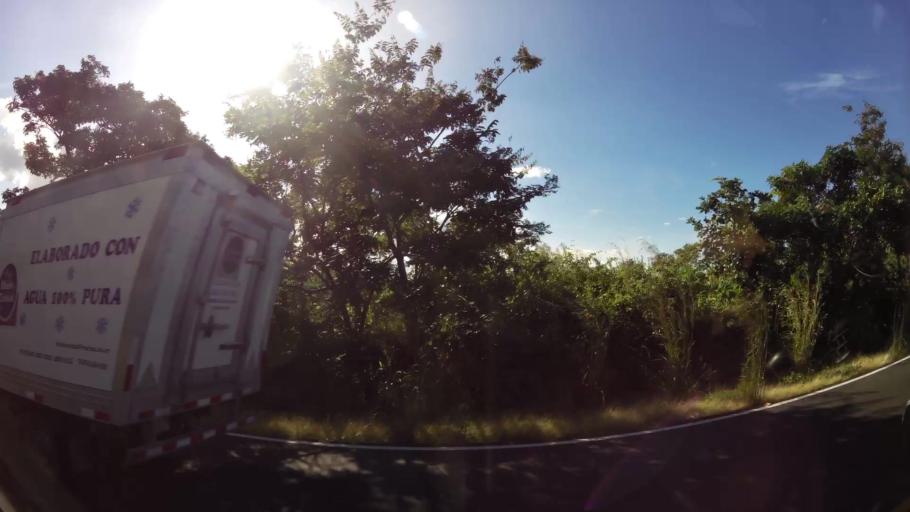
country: CR
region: Guanacaste
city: Sardinal
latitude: 10.5807
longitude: -85.6392
